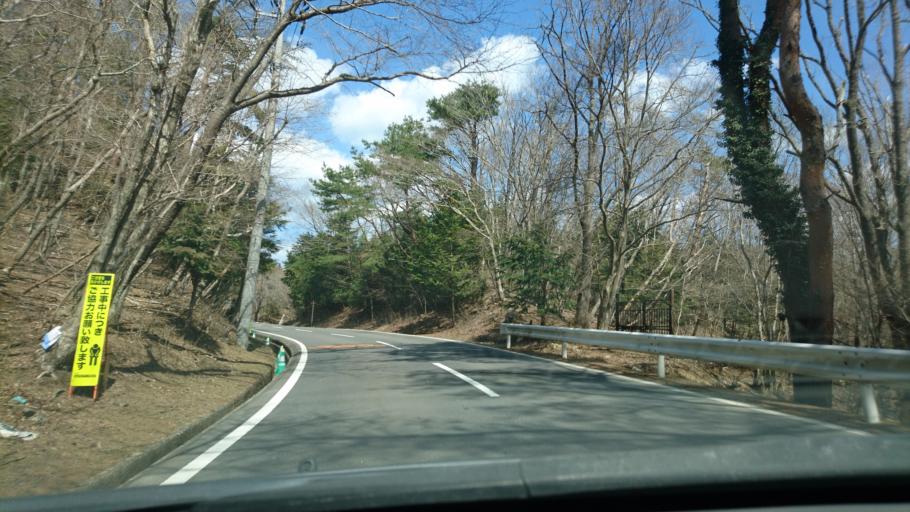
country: JP
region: Miyagi
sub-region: Oshika Gun
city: Onagawa Cho
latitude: 38.4759
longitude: 141.4930
